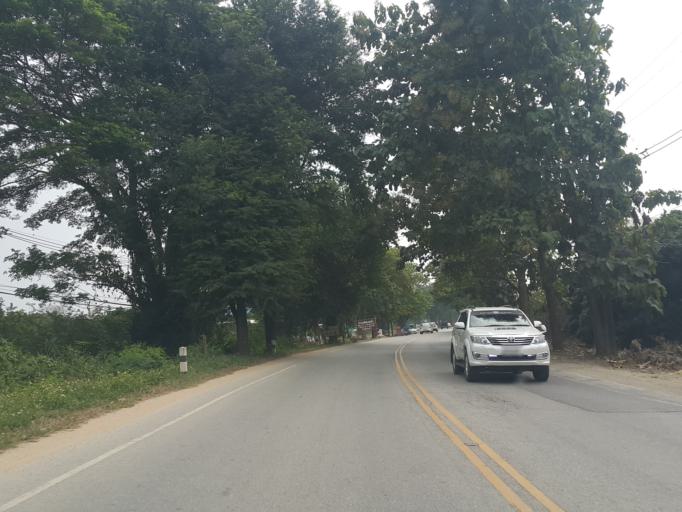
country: TH
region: Chiang Mai
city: Mae Taeng
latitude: 18.9920
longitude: 98.9783
